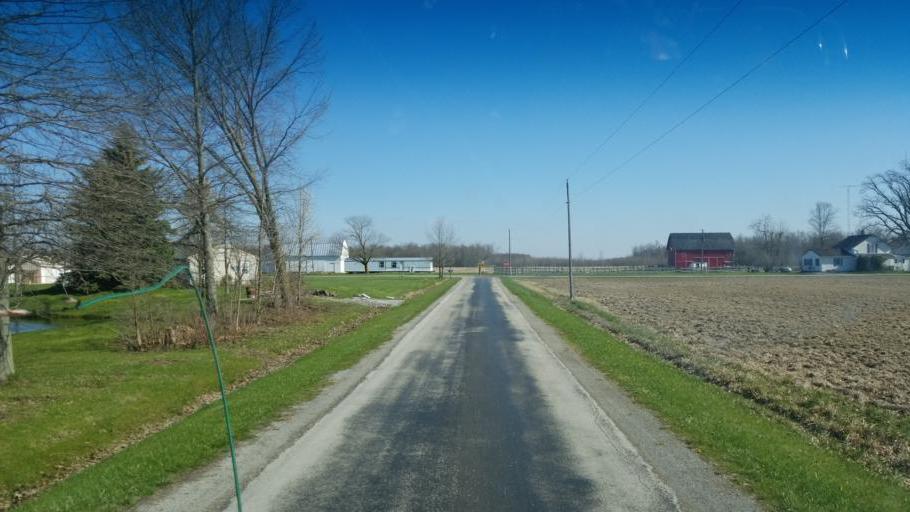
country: US
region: Ohio
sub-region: Hardin County
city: Forest
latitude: 40.7157
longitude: -83.4453
